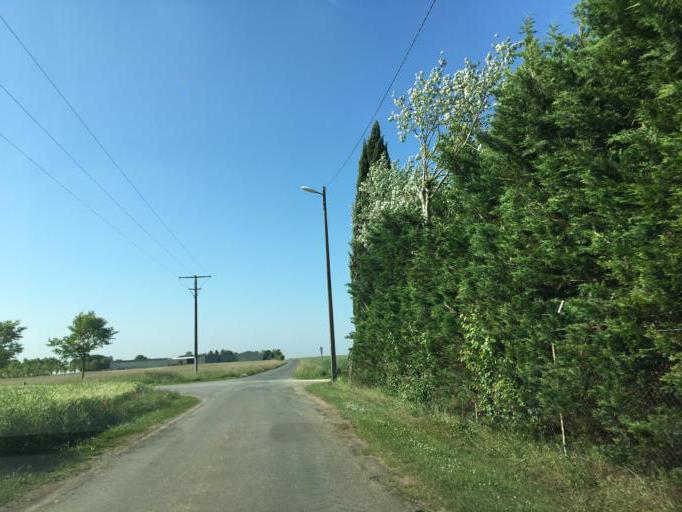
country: FR
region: Poitou-Charentes
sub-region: Departement des Deux-Sevres
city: Beauvoir-sur-Niort
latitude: 46.0888
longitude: -0.5062
